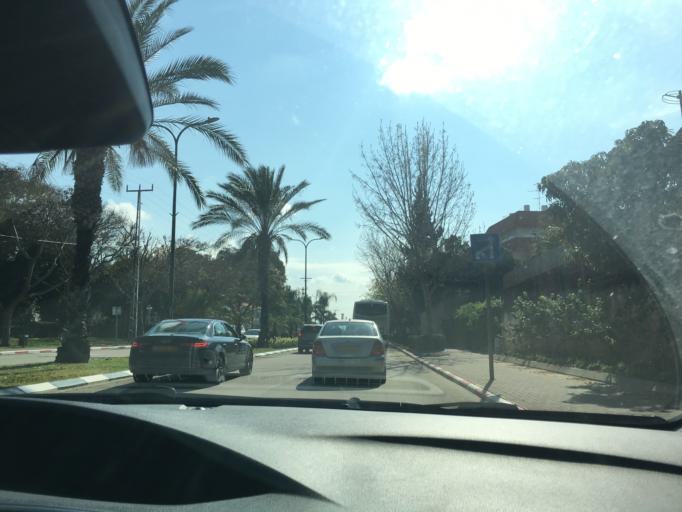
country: IL
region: Tel Aviv
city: Ramat HaSharon
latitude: 32.1621
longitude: 34.8528
